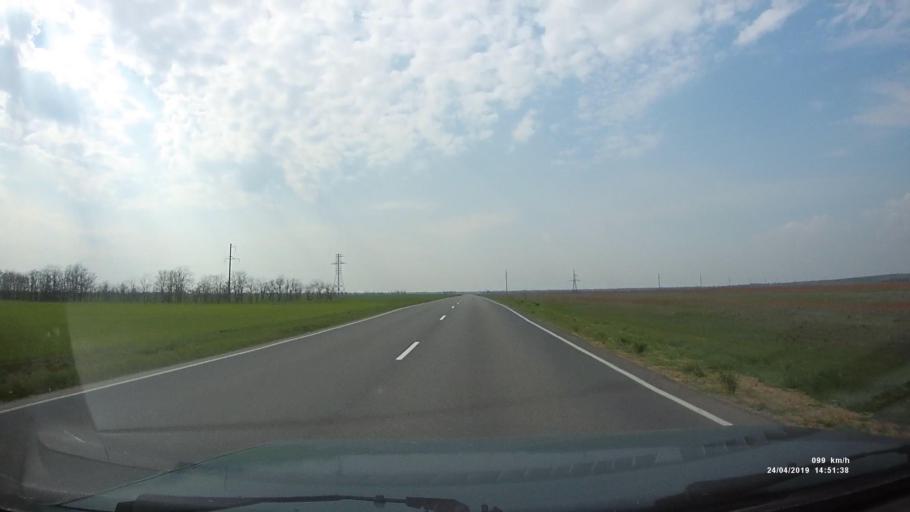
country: RU
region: Rostov
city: Remontnoye
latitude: 46.5264
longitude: 43.6968
